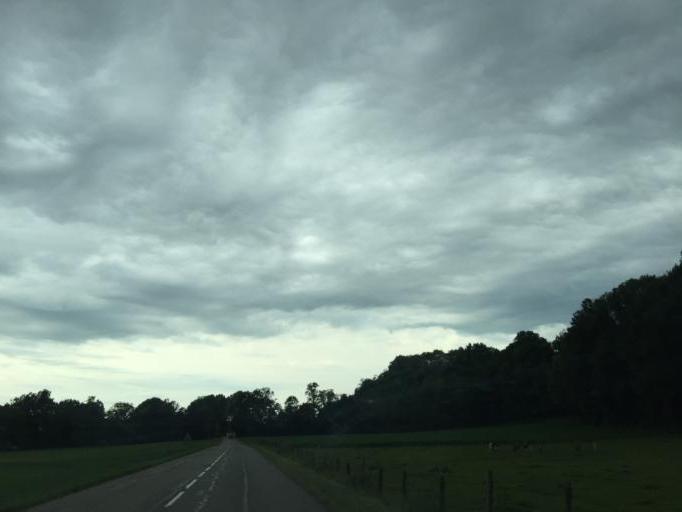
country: FR
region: Rhone-Alpes
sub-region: Departement de la Savoie
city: Le Pont-de-Beauvoisin
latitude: 45.5615
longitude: 5.6742
